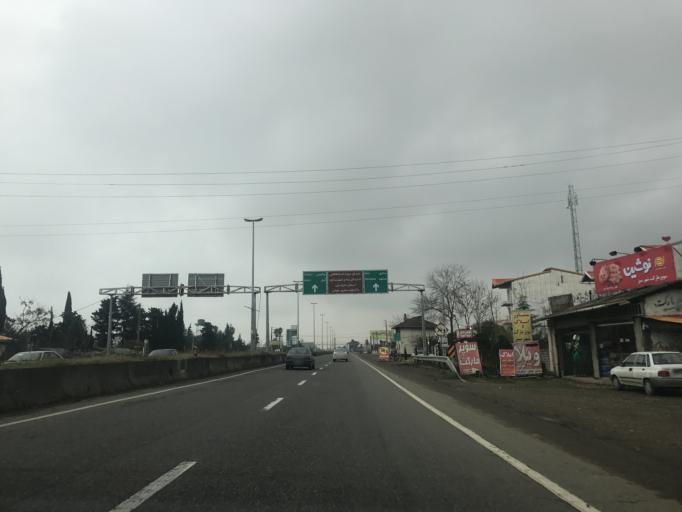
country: IR
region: Mazandaran
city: Ramsar
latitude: 36.9617
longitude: 50.5958
